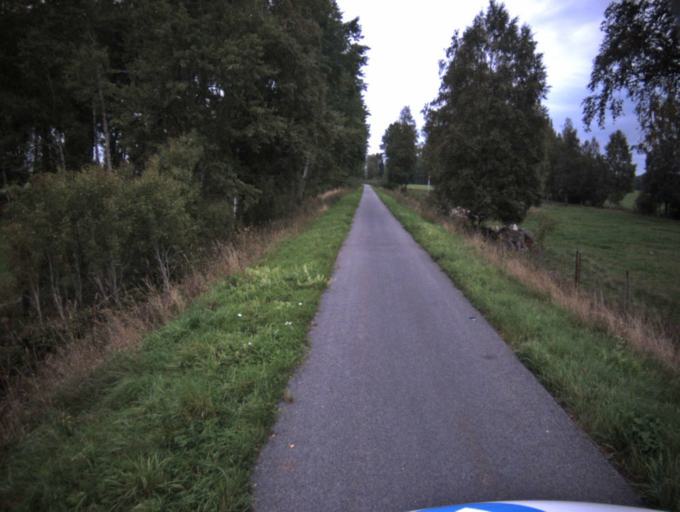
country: SE
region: Vaestra Goetaland
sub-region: Ulricehamns Kommun
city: Ulricehamn
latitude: 57.9498
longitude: 13.5046
